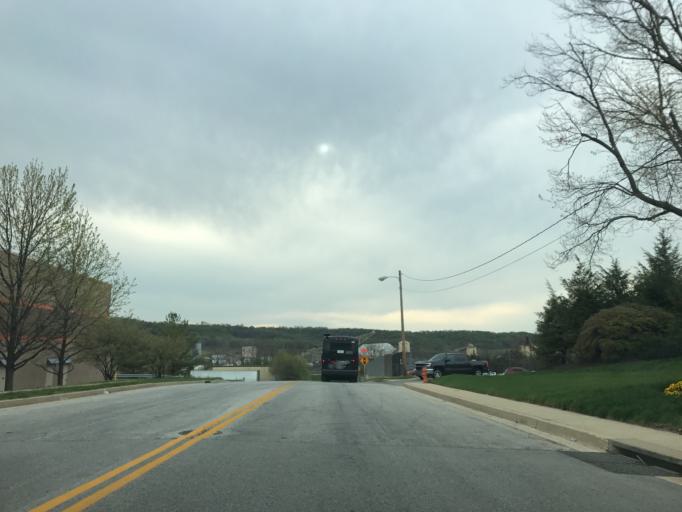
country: US
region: Maryland
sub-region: Baltimore County
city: Cockeysville
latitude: 39.4659
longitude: -76.6418
